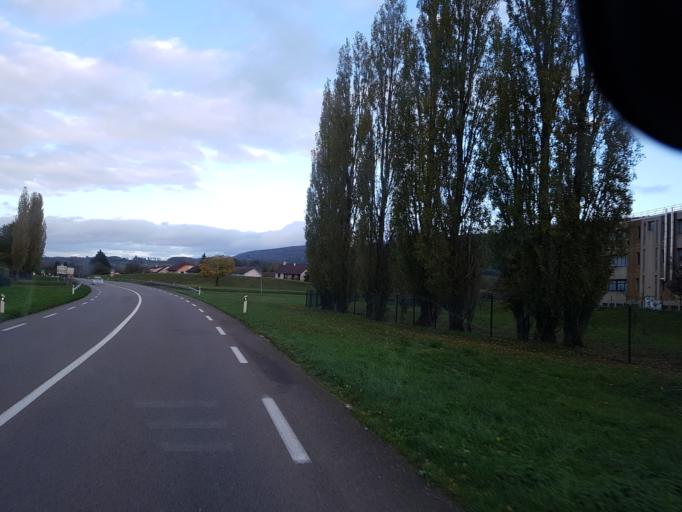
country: FR
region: Franche-Comte
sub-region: Departement du Jura
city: Poligny
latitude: 46.8373
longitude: 5.6967
